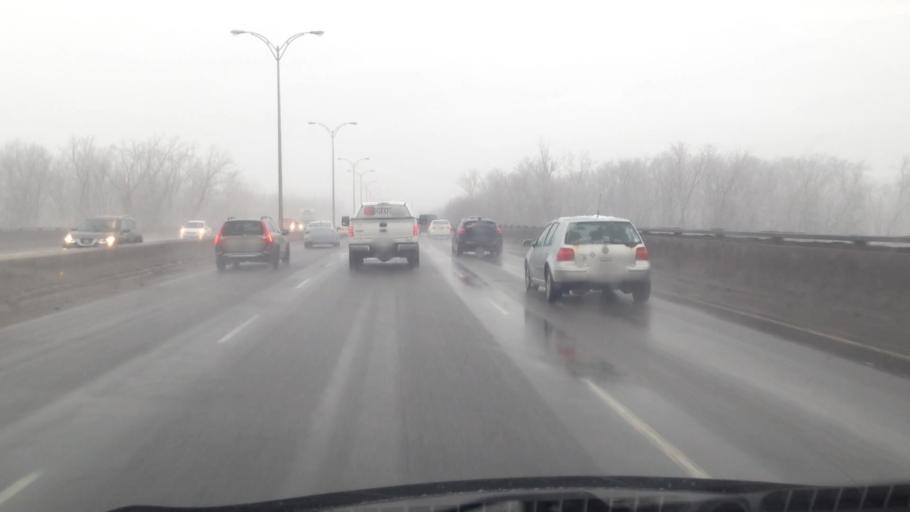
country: CA
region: Quebec
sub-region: Laurentides
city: Boisbriand
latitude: 45.6095
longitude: -73.8116
